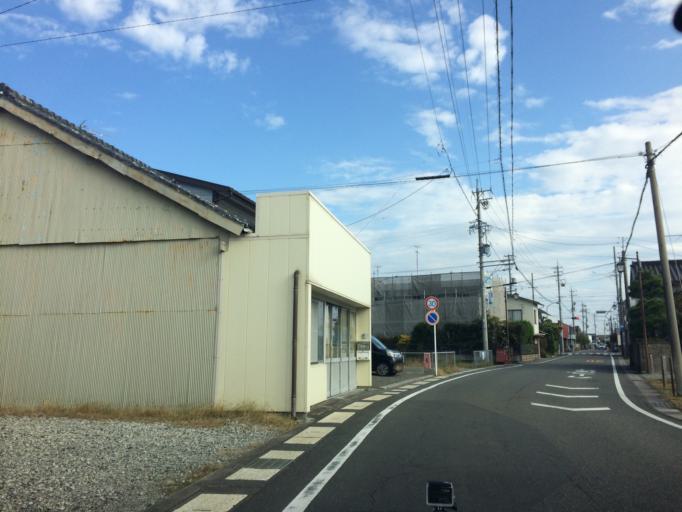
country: JP
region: Shizuoka
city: Sagara
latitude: 34.7376
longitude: 138.2197
